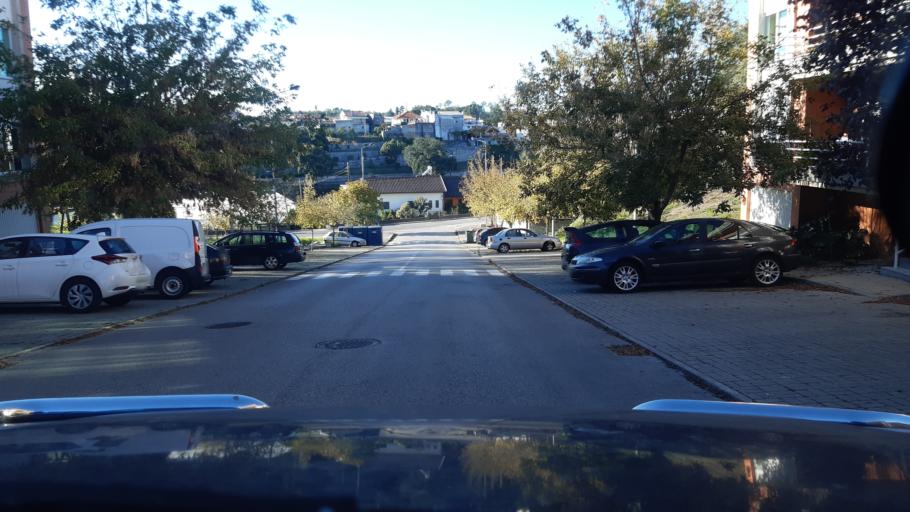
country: PT
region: Aveiro
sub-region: Agueda
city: Agueda
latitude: 40.5541
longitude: -8.4395
